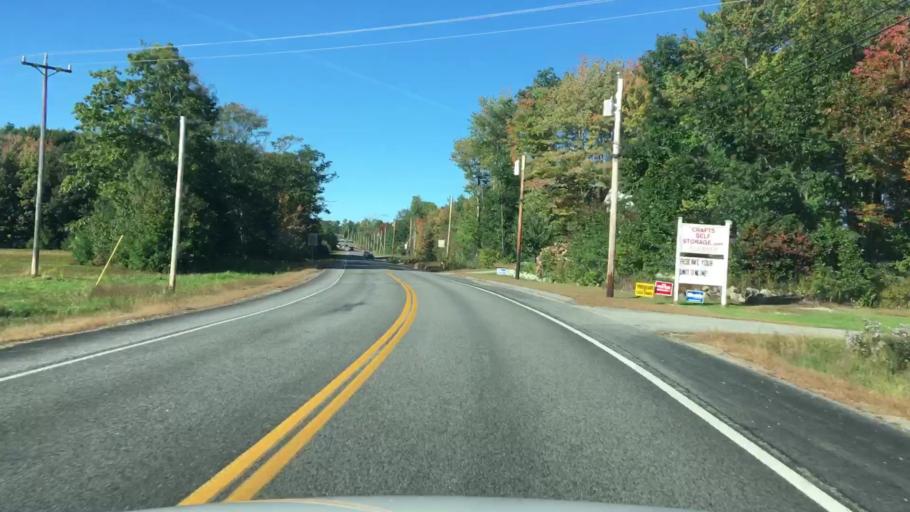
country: US
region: Maine
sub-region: Androscoggin County
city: Lisbon Falls
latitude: 44.0168
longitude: -70.0675
